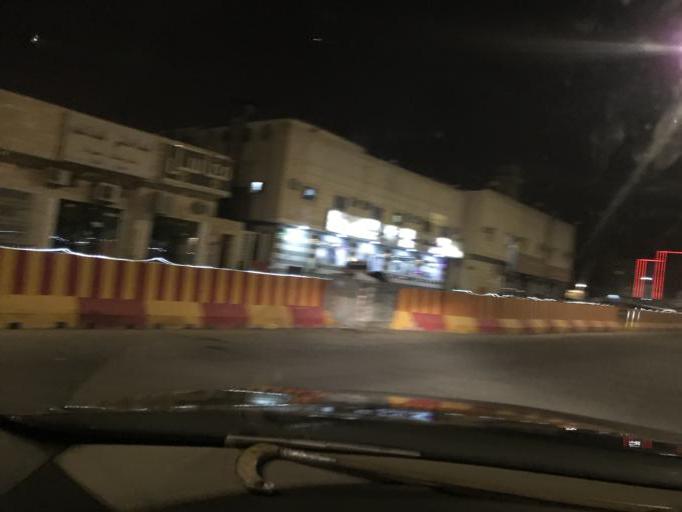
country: SA
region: Ar Riyad
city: Riyadh
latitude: 24.8013
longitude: 46.7075
